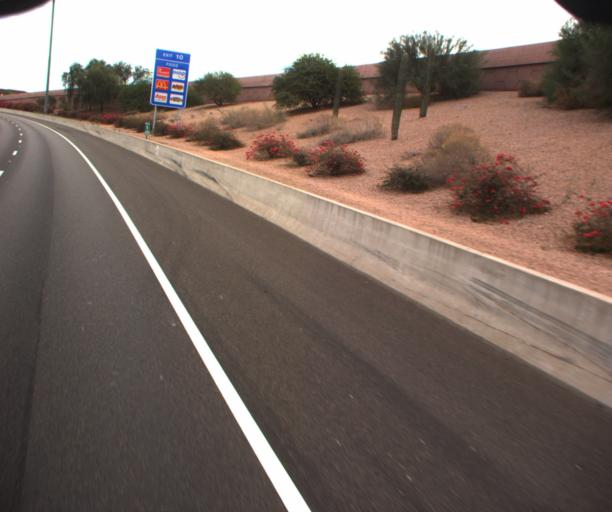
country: US
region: Arizona
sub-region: Maricopa County
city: Tempe
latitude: 33.4333
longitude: -111.8880
